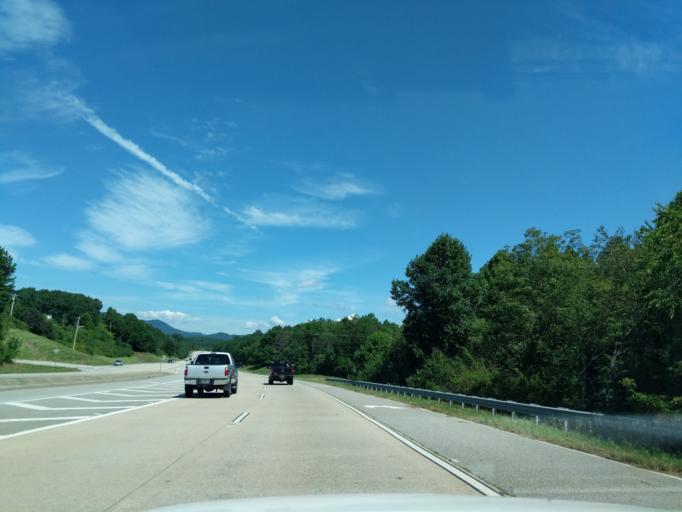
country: US
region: Georgia
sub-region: Union County
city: Blairsville
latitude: 34.8608
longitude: -84.0007
